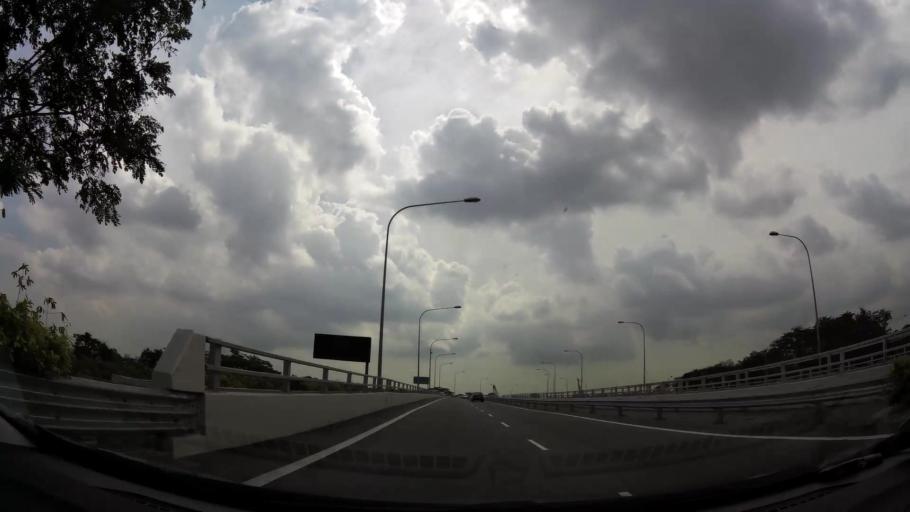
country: MY
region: Johor
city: Kampung Pasir Gudang Baru
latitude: 1.4004
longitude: 103.8566
